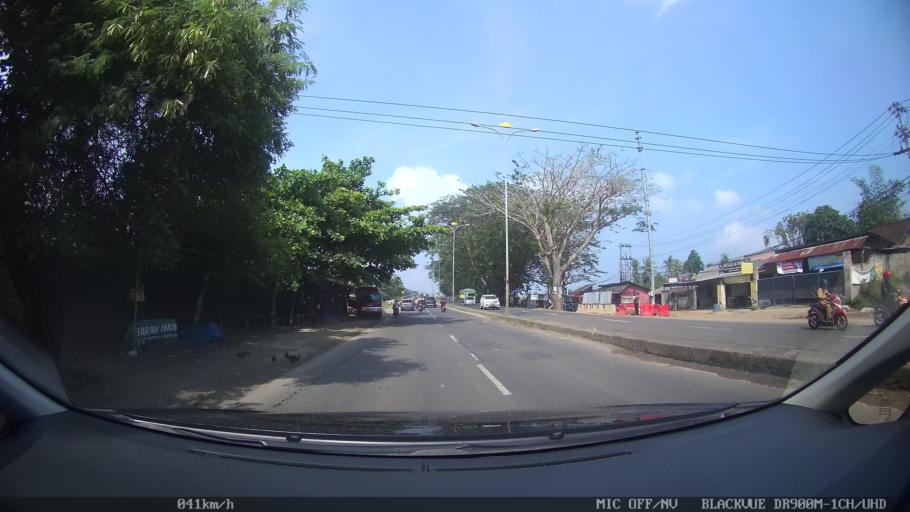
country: ID
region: Lampung
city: Kedaton
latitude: -5.3585
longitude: 105.2458
